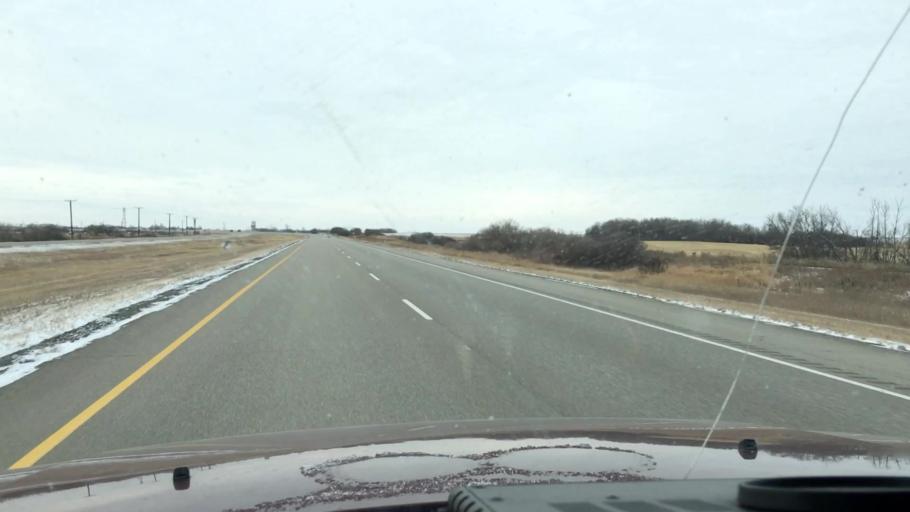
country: CA
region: Saskatchewan
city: Watrous
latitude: 51.3854
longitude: -106.1633
